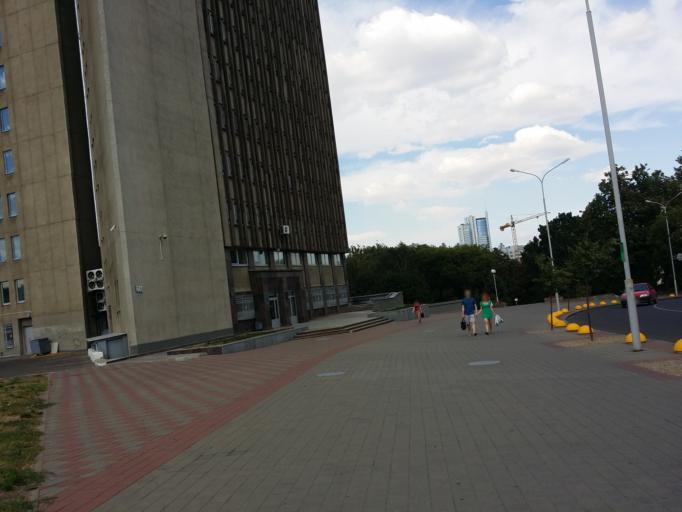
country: BY
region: Minsk
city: Minsk
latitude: 53.8993
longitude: 27.5494
